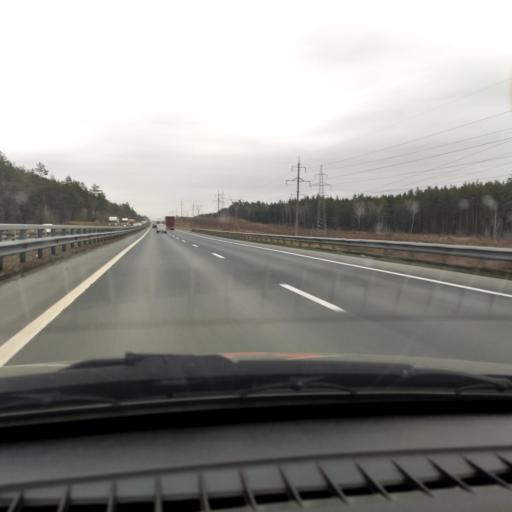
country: RU
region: Samara
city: Povolzhskiy
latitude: 53.5170
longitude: 49.7365
